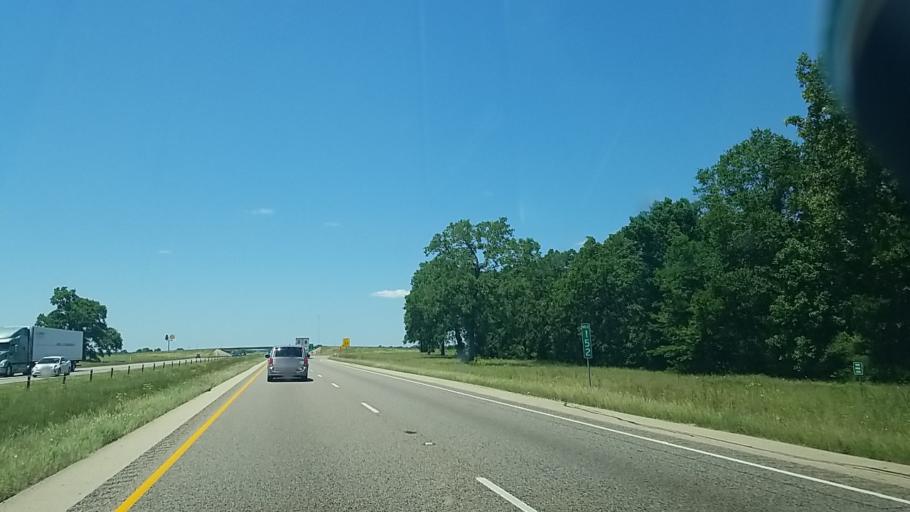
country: US
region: Texas
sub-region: Madison County
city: Madisonville
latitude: 31.0876
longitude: -95.9593
